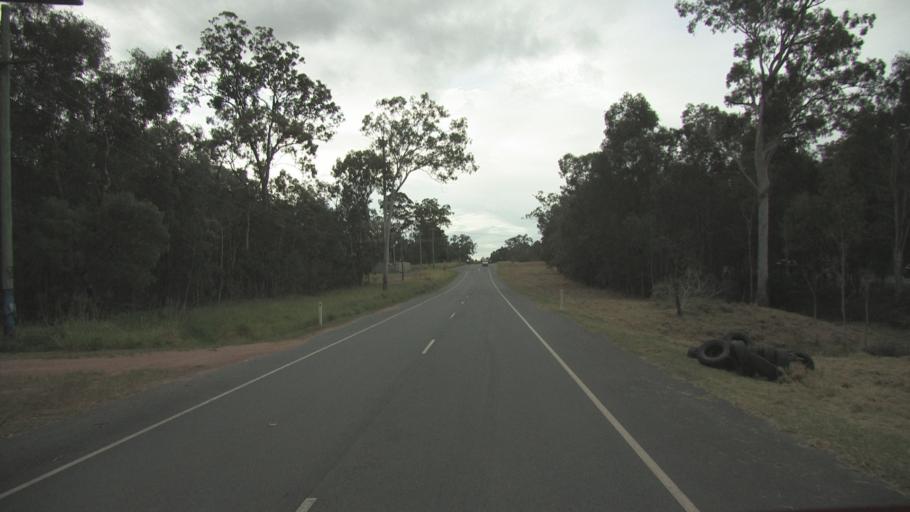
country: AU
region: Queensland
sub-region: Logan
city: Park Ridge South
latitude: -27.7388
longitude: 153.0264
